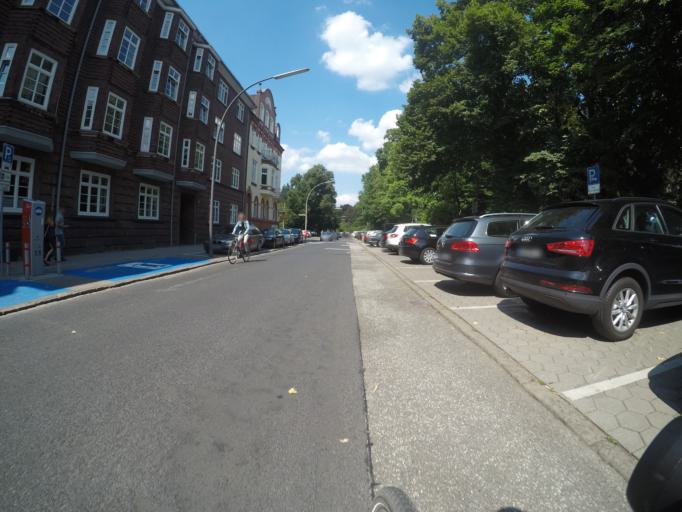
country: DE
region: Hamburg
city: Bergedorf
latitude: 53.4880
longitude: 10.2154
